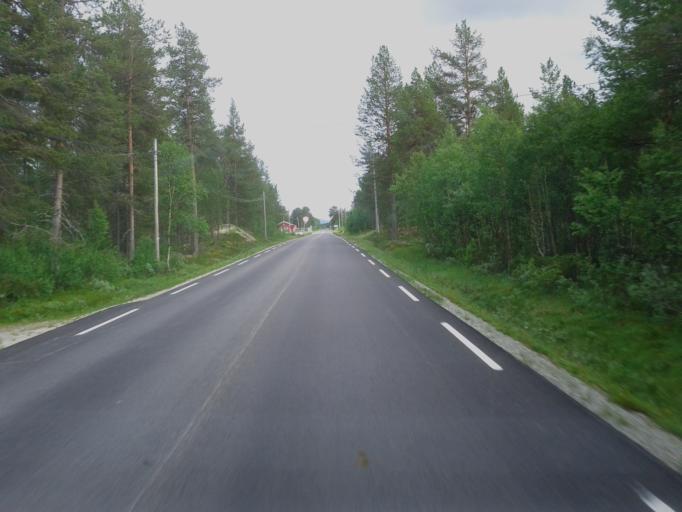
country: NO
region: Sor-Trondelag
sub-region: Roros
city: Roros
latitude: 62.2886
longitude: 11.7329
